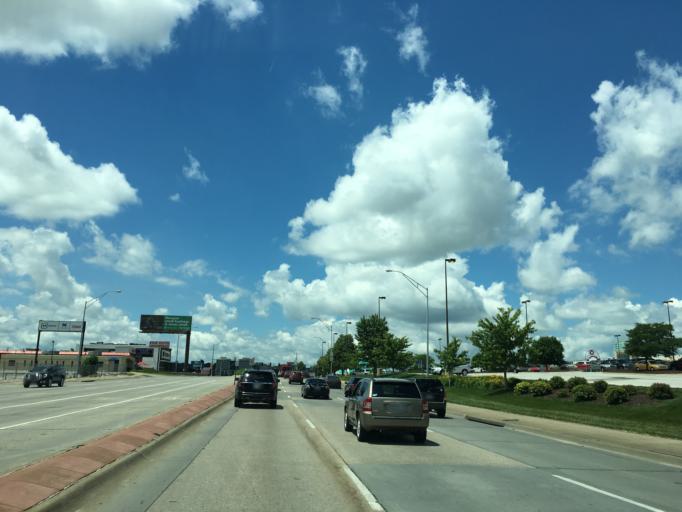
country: US
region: Nebraska
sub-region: Douglas County
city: Ralston
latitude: 41.2597
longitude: -96.0241
